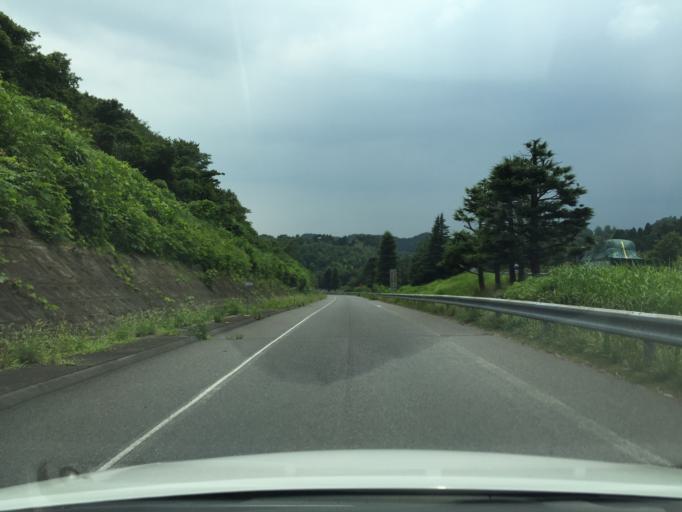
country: JP
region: Fukushima
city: Iwaki
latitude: 37.0045
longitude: 140.8113
